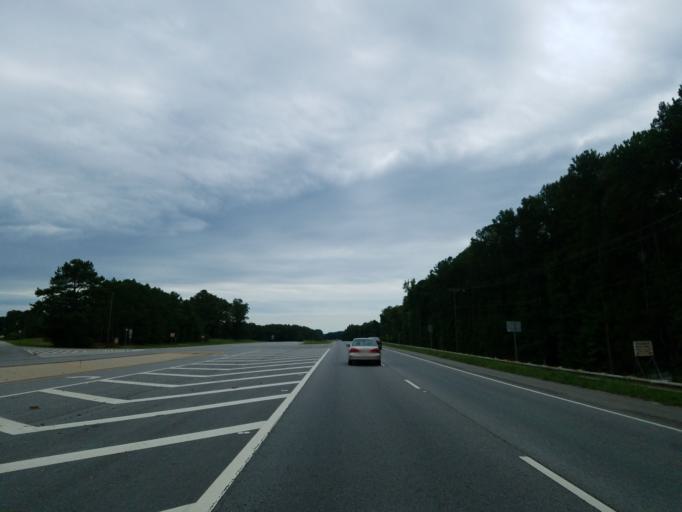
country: US
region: Georgia
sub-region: Spalding County
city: Griffin
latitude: 33.1621
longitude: -84.2572
